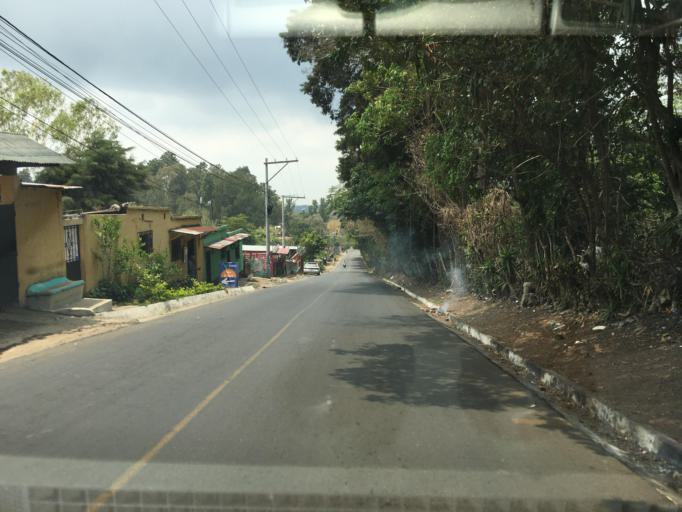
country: GT
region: Escuintla
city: San Vicente Pacaya
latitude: 14.3422
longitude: -90.5708
